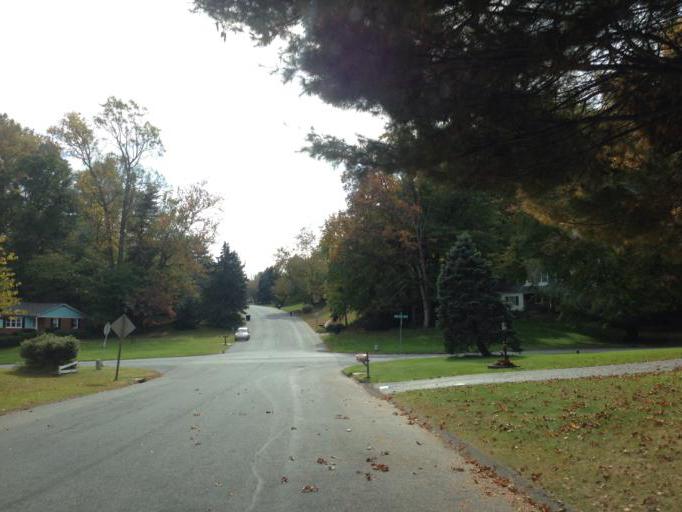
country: US
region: Maryland
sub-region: Howard County
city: Columbia
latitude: 39.2907
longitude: -76.8475
